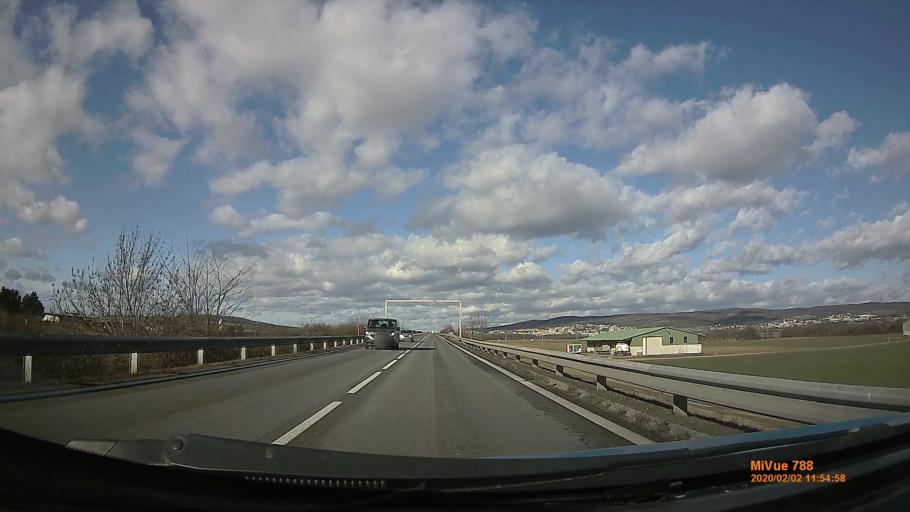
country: AT
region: Burgenland
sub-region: Eisenstadt-Umgebung
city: Wulkaprodersdorf
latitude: 47.8003
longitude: 16.5126
